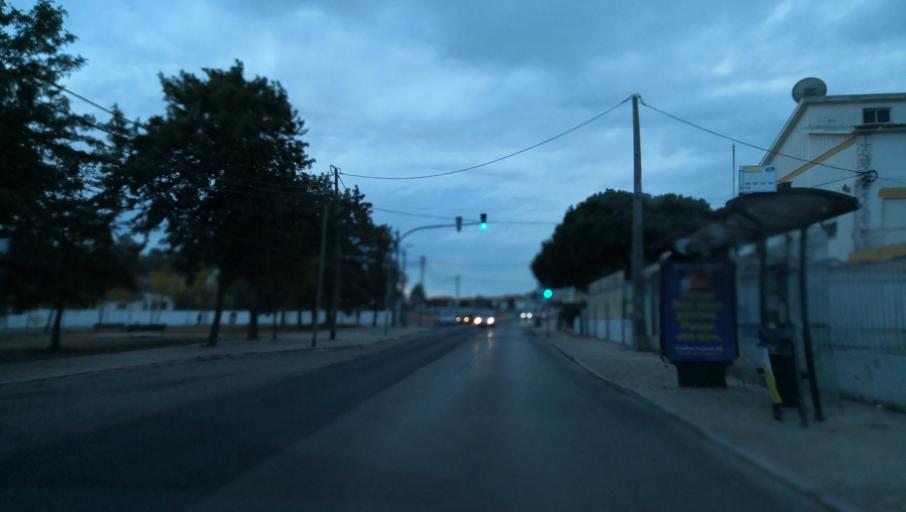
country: PT
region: Setubal
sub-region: Almada
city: Charneca
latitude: 38.6055
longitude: -9.1863
